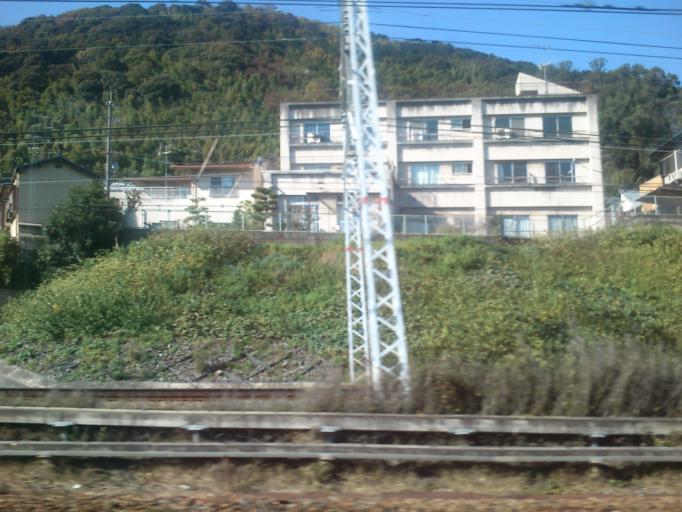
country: JP
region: Kyoto
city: Yawata
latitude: 34.9002
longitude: 135.6851
